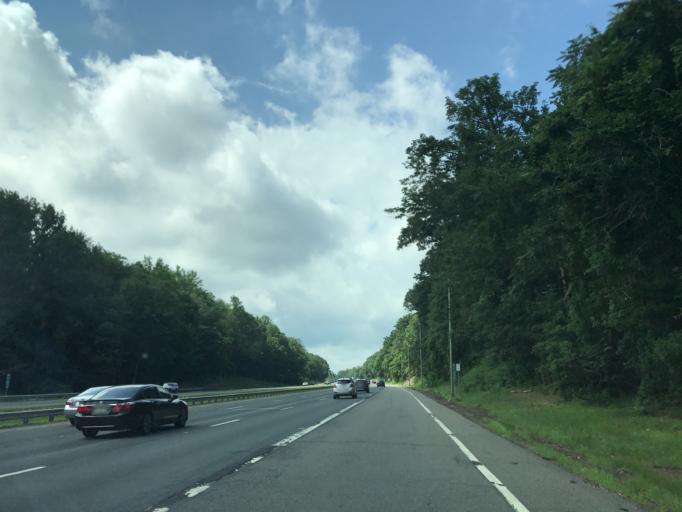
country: US
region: New Jersey
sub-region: Morris County
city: Mountain Lakes
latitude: 40.8850
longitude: -74.4181
